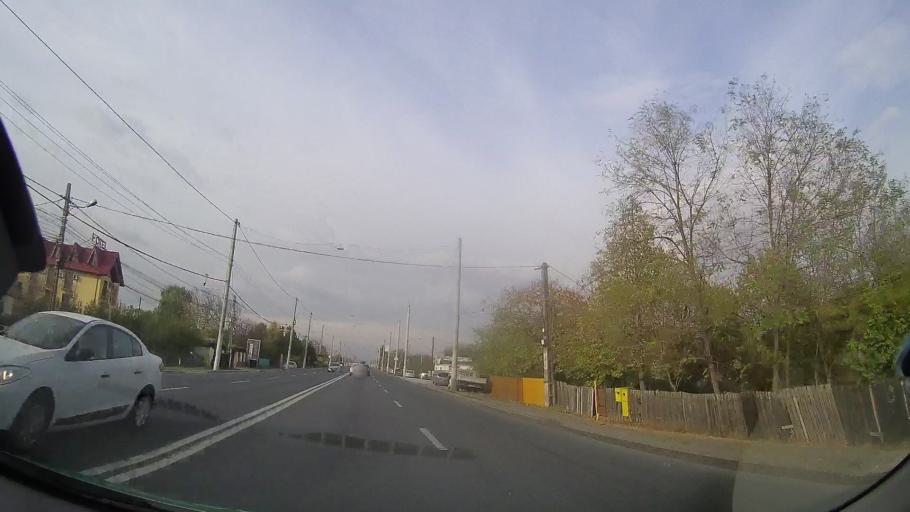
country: RO
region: Prahova
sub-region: Comuna Barcanesti
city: Barcanesti
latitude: 44.8893
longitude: 26.0452
